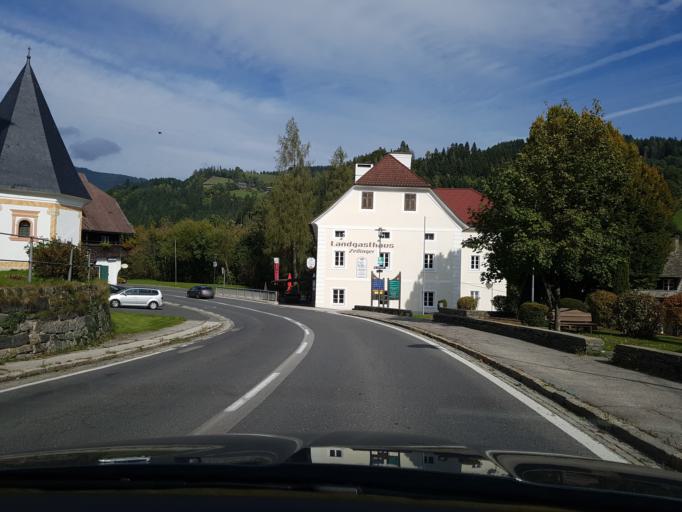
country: AT
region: Carinthia
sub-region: Politischer Bezirk Feldkirchen
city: Himmelberg
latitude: 46.7483
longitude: 14.0374
